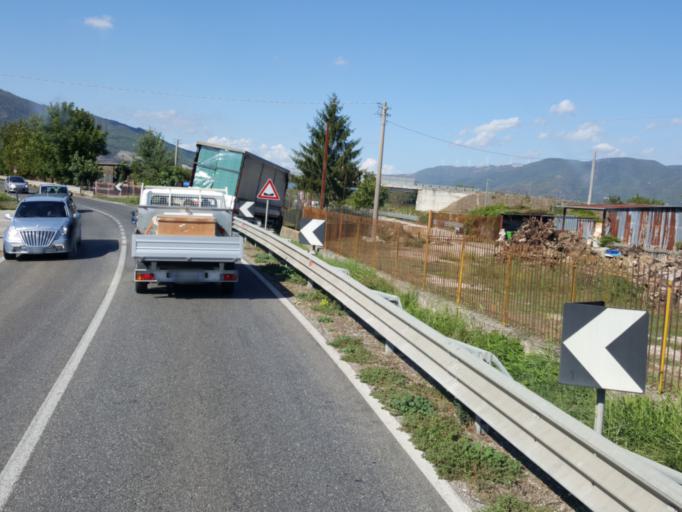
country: IT
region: Campania
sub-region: Provincia di Caserta
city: Presenzano
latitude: 41.3539
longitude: 14.1046
